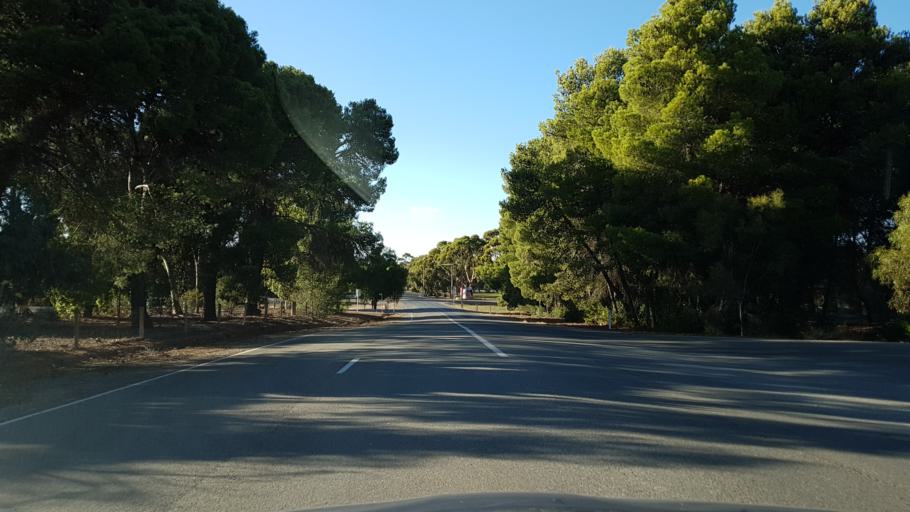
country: AU
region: South Australia
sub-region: Port Pirie City and Dists
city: Crystal Brook
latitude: -33.2710
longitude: 138.3524
